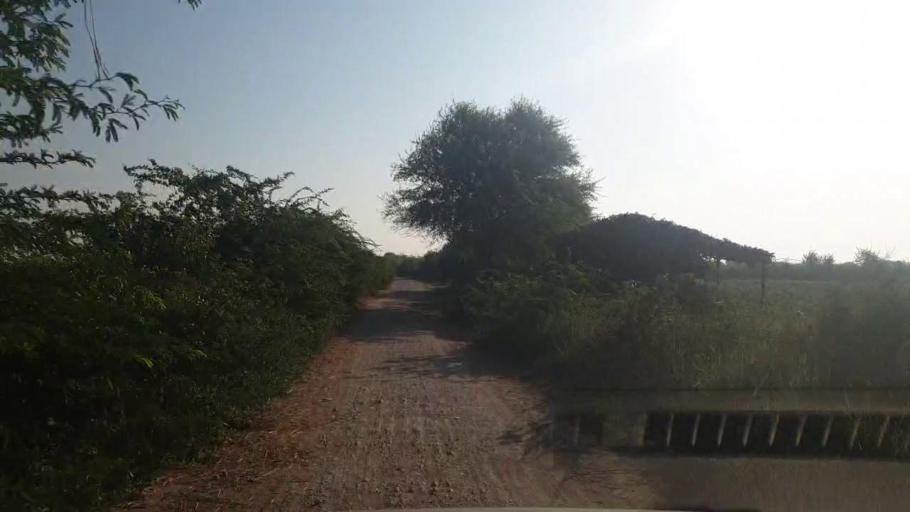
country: PK
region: Sindh
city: Badin
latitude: 24.7340
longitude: 68.8764
